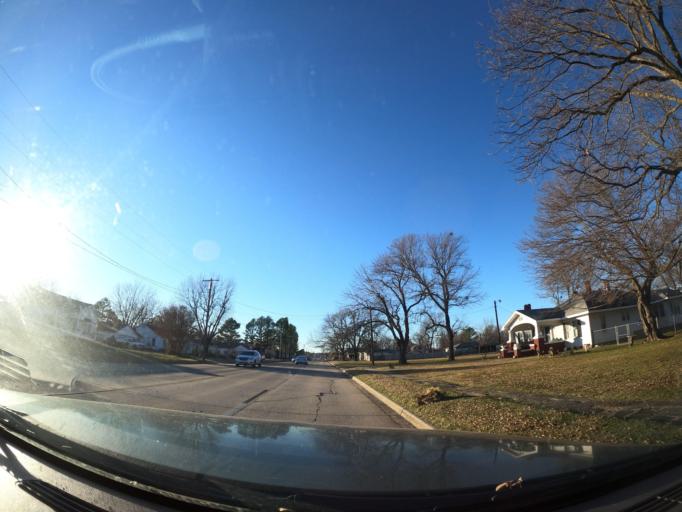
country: US
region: Oklahoma
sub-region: Pittsburg County
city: Hartshorne
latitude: 34.8430
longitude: -95.5494
